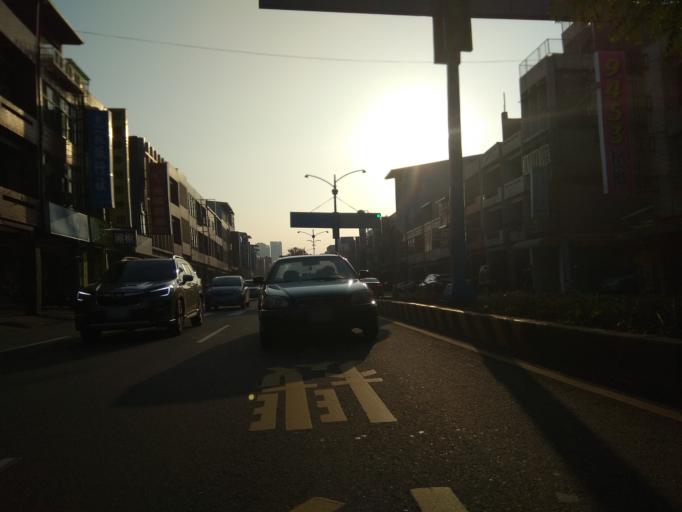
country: TW
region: Taiwan
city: Daxi
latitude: 24.9219
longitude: 121.1865
